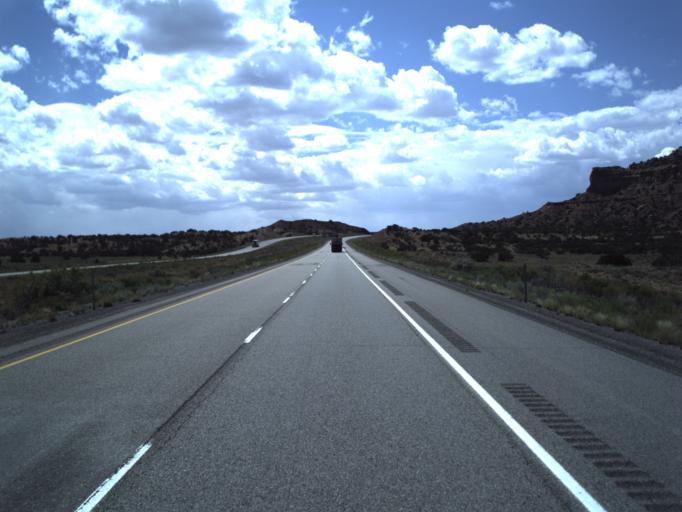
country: US
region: Utah
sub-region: Emery County
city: Castle Dale
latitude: 38.8695
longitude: -110.6977
